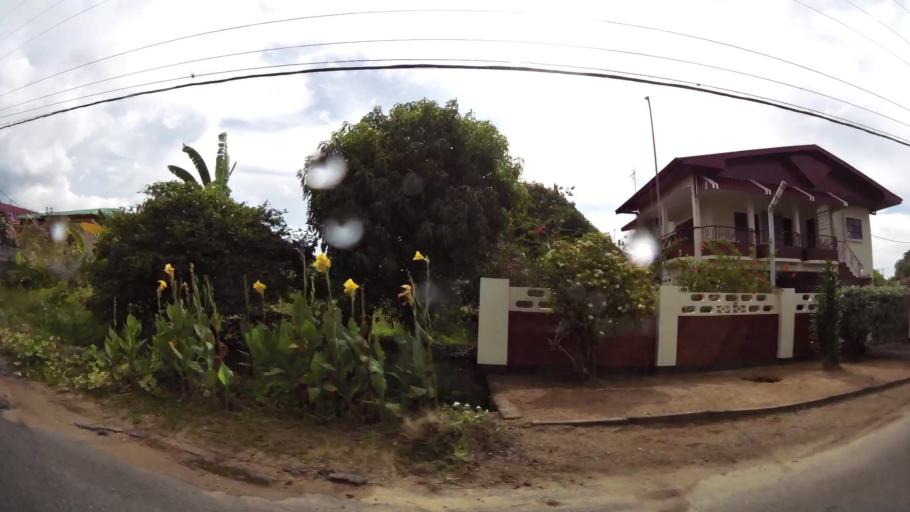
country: SR
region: Paramaribo
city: Paramaribo
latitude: 5.8454
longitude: -55.1928
